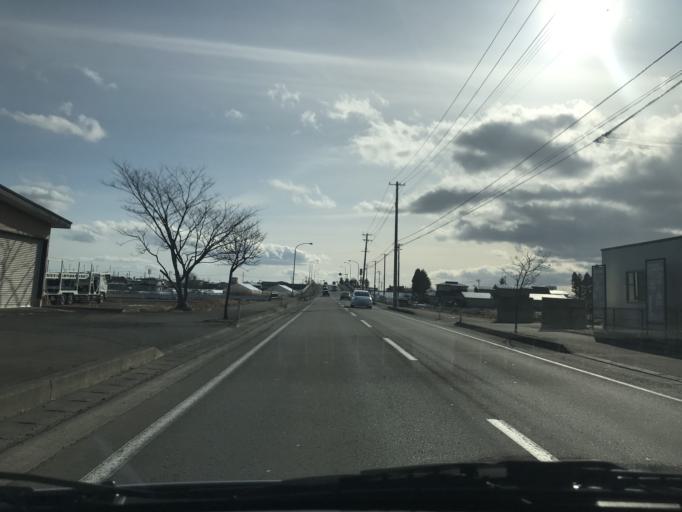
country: JP
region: Iwate
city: Kitakami
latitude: 39.2985
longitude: 141.0982
